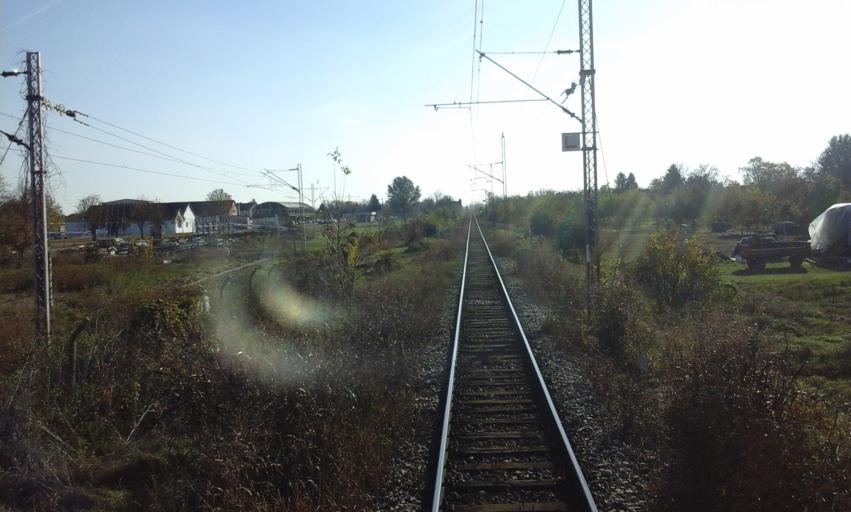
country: RS
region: Autonomna Pokrajina Vojvodina
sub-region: Severnobacki Okrug
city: Backa Topola
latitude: 45.8089
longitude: 19.6482
